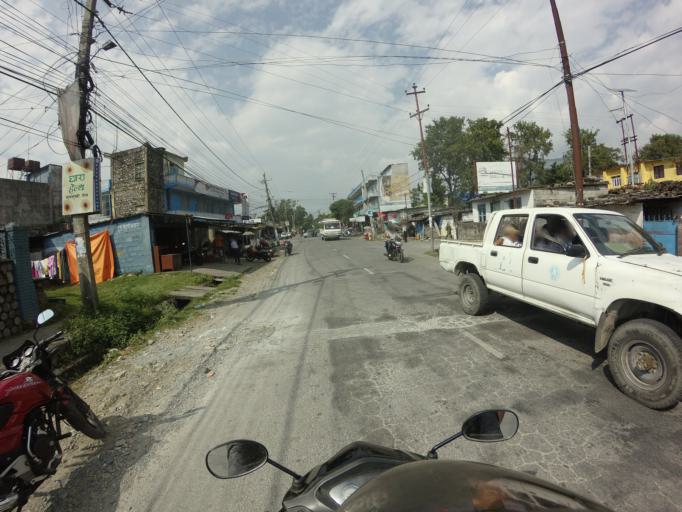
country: NP
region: Western Region
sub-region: Gandaki Zone
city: Pokhara
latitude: 28.2116
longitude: 84.0000
